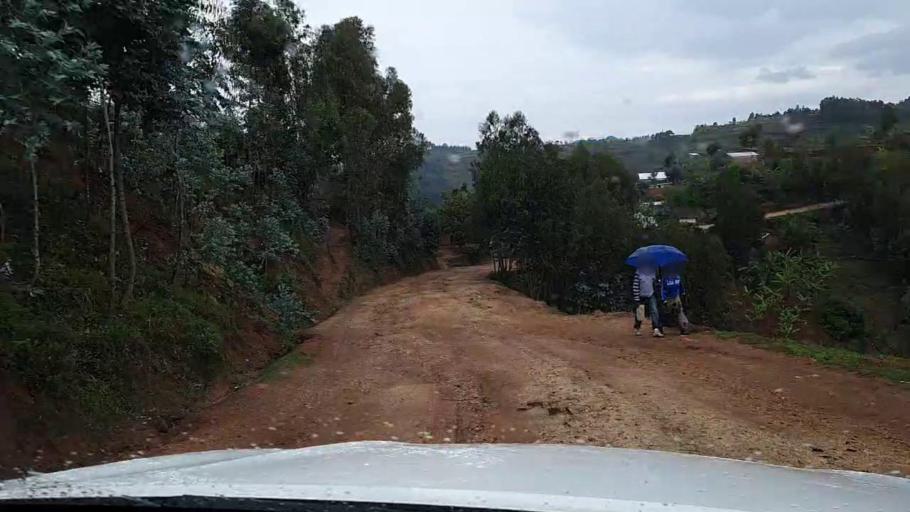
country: RW
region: Southern Province
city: Nzega
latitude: -2.4647
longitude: 29.4951
